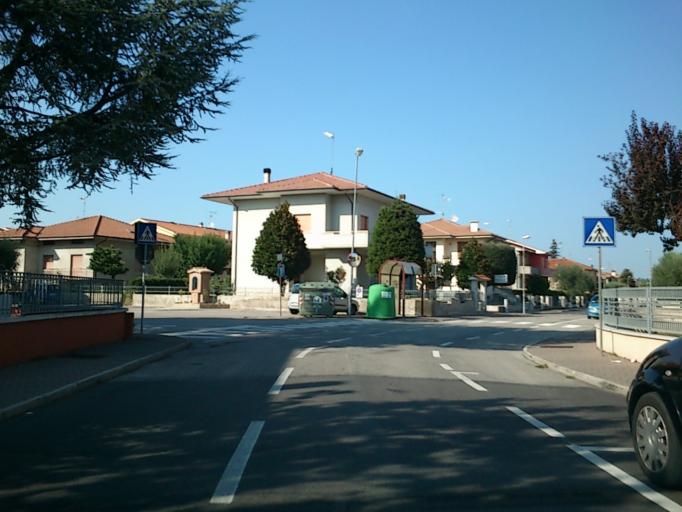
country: IT
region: The Marches
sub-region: Provincia di Pesaro e Urbino
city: Lucrezia
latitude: 43.7777
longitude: 12.9421
